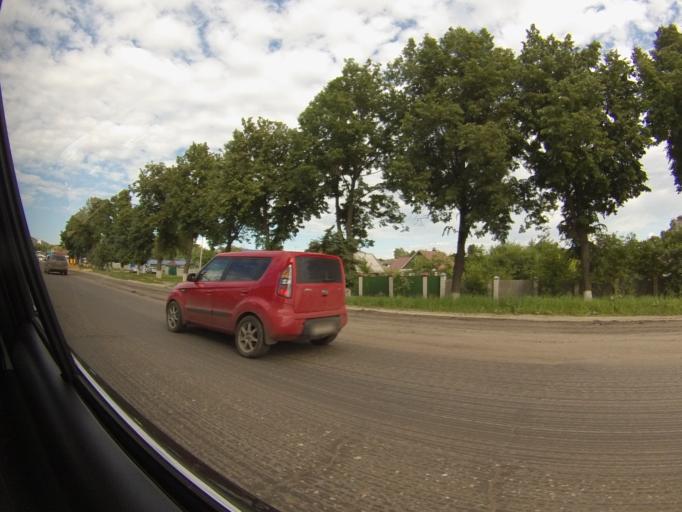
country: RU
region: Orjol
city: Mtsensk
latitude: 53.2856
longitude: 36.5888
